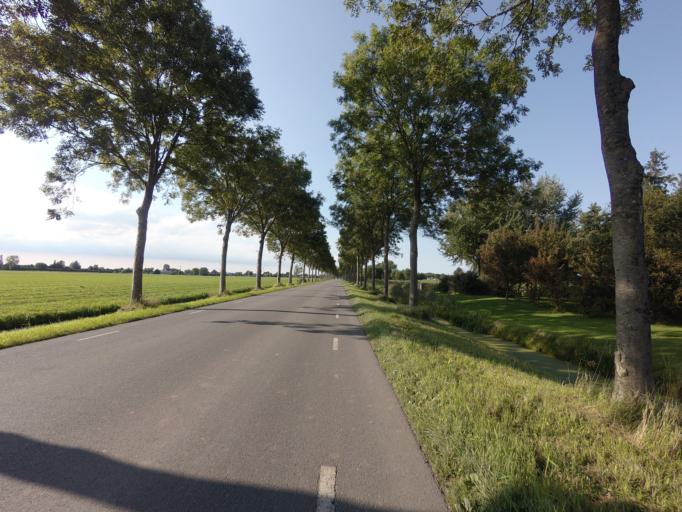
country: NL
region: North Holland
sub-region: Gemeente Hoorn
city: Hoorn
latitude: 52.6715
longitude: 5.1403
